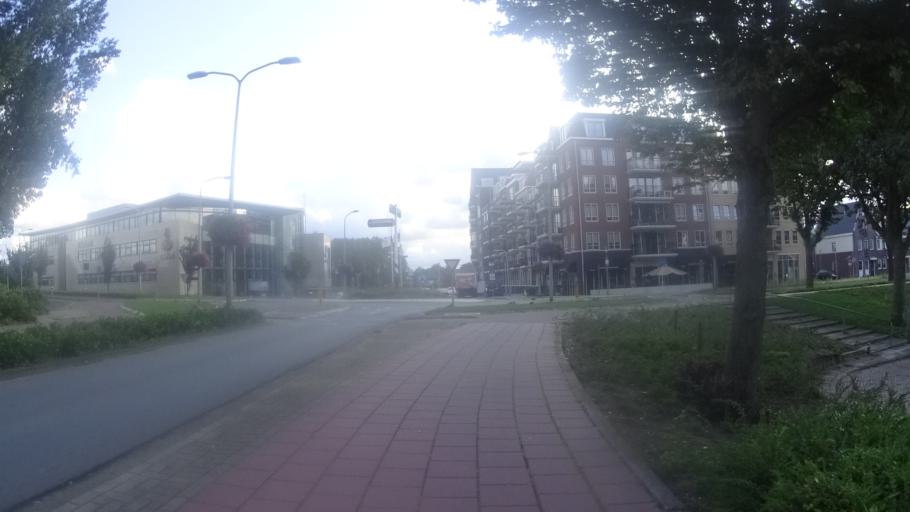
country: NL
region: South Holland
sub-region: Gemeente Katwijk
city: Katwijk aan Zee
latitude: 52.2044
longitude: 4.4091
